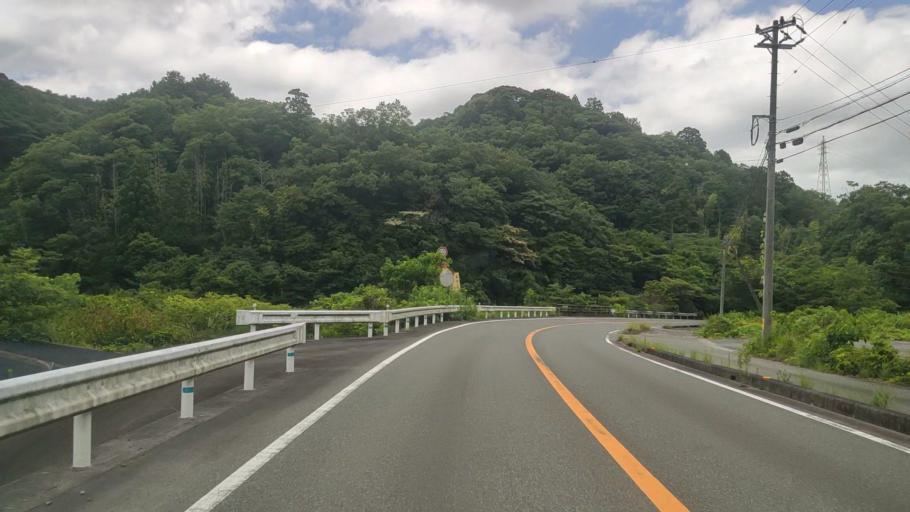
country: JP
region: Mie
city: Ise
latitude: 34.3538
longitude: 136.7410
